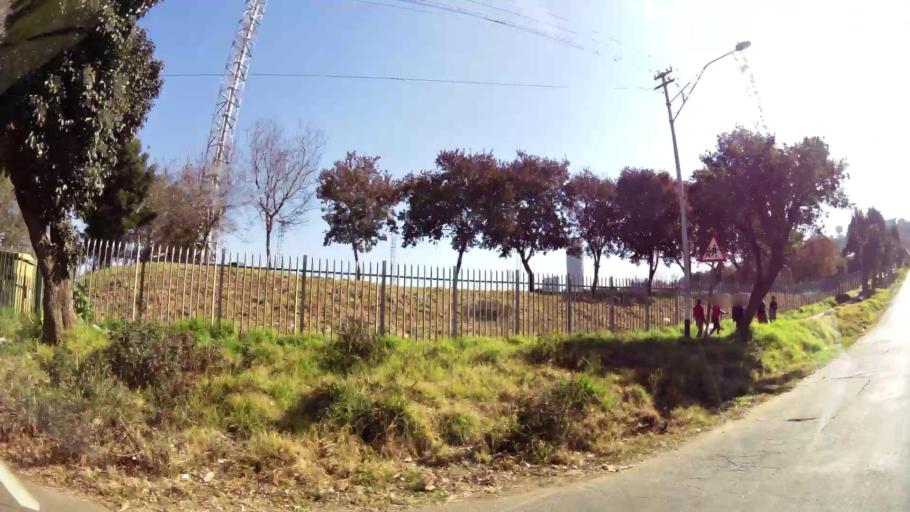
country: ZA
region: Gauteng
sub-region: City of Johannesburg Metropolitan Municipality
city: Johannesburg
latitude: -26.1942
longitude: 28.0676
